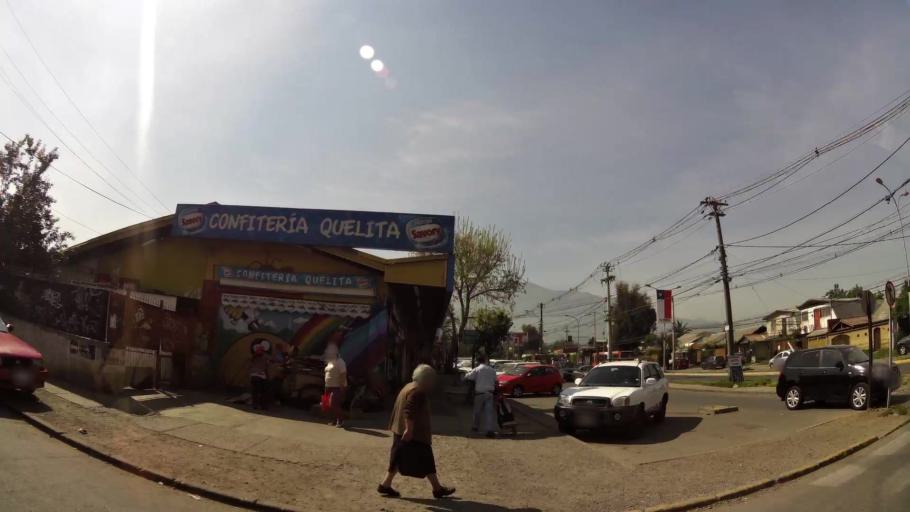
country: CL
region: Santiago Metropolitan
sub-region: Provincia de Santiago
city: Villa Presidente Frei, Nunoa, Santiago, Chile
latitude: -33.5060
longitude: -70.5790
